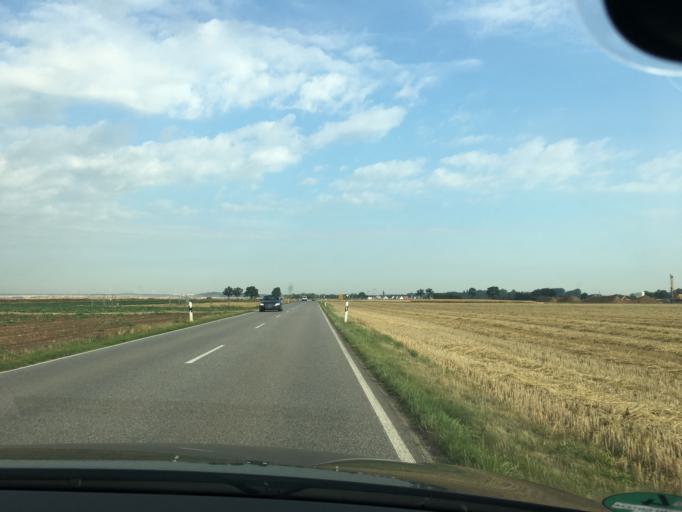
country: DE
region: North Rhine-Westphalia
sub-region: Regierungsbezirk Koln
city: Inden
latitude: 50.8615
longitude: 6.4152
